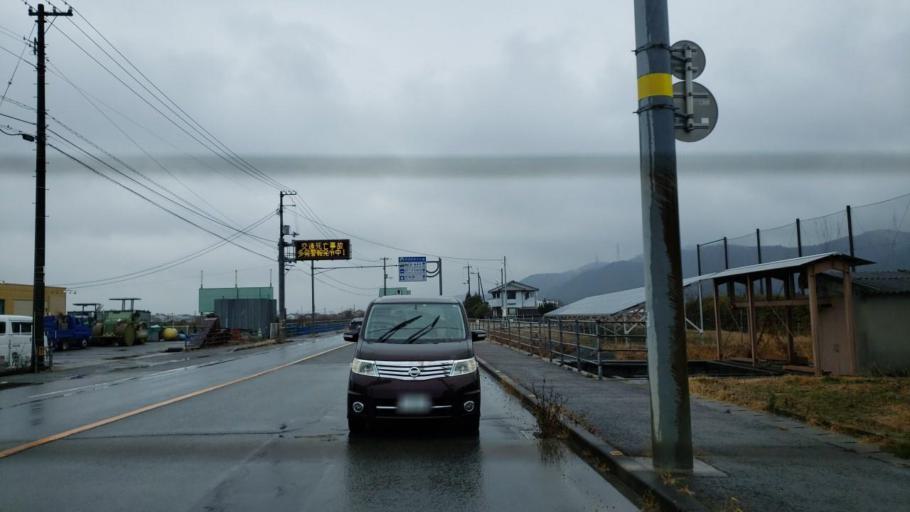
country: JP
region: Tokushima
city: Narutocho-mitsuishi
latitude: 34.1657
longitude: 134.5784
